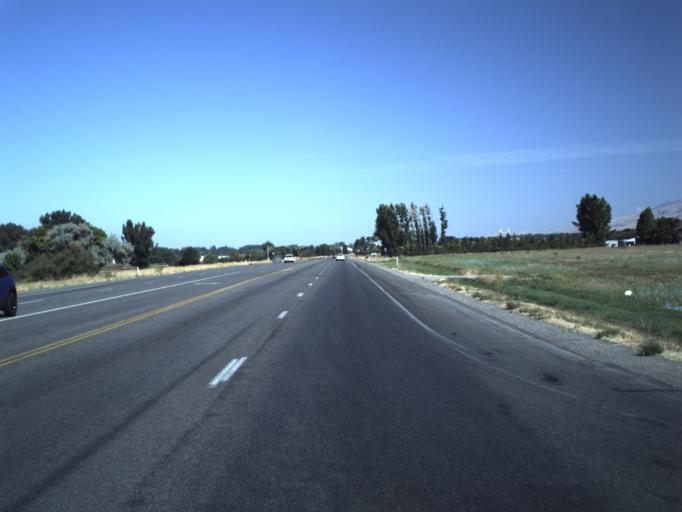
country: US
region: Utah
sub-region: Cache County
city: Millville
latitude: 41.6895
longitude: -111.8341
